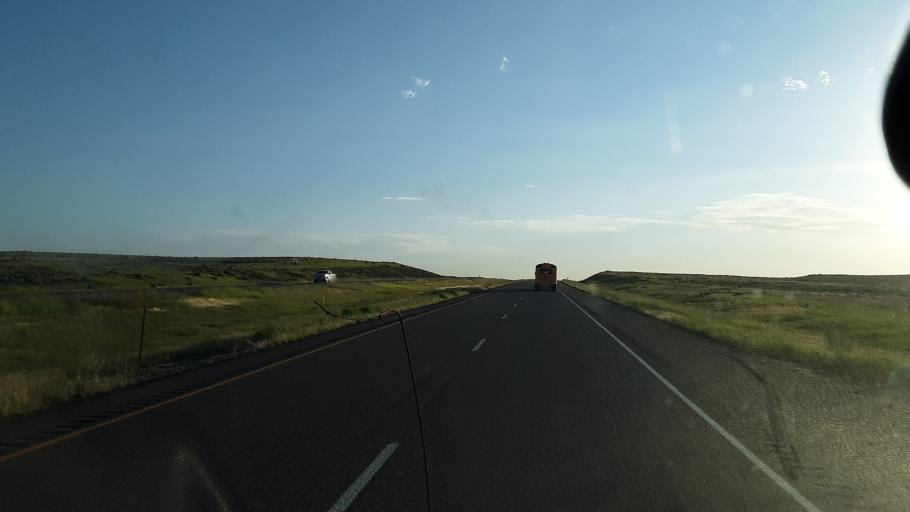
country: US
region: Montana
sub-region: Big Horn County
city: Hardin
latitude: 45.7445
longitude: -107.7098
